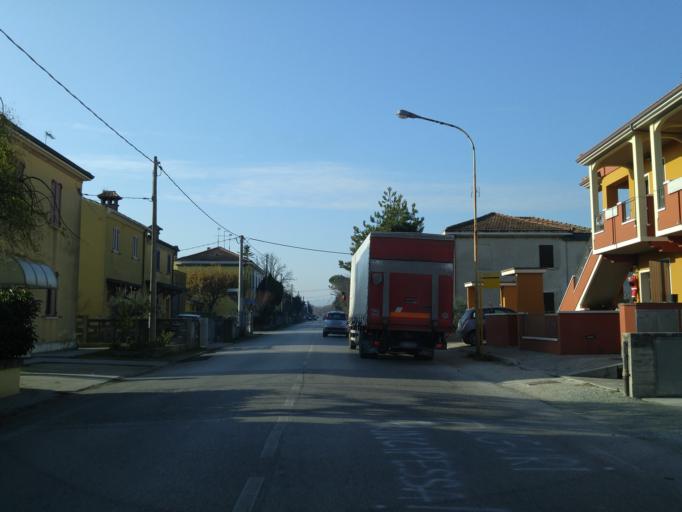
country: IT
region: The Marches
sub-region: Provincia di Pesaro e Urbino
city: Cuccurano
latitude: 43.7962
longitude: 12.9593
